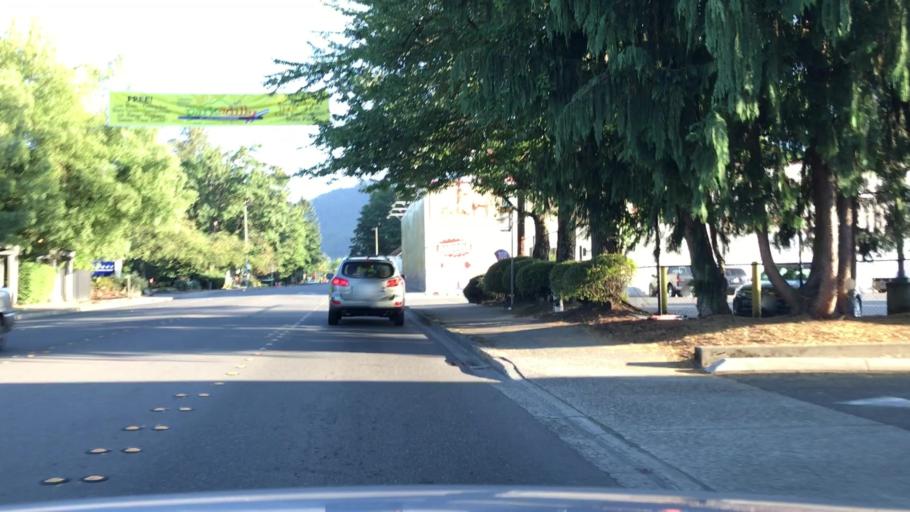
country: US
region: Washington
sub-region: King County
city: Issaquah
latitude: 47.5370
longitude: -122.0365
